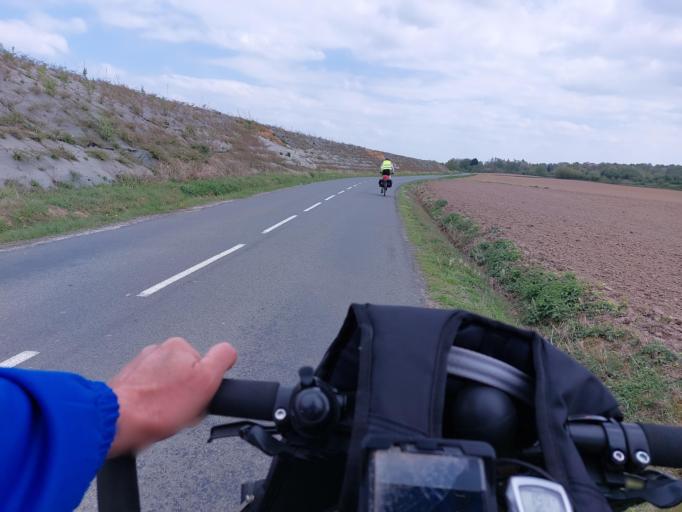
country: FR
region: Nord-Pas-de-Calais
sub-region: Departement du Nord
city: La Longueville
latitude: 50.2806
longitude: 3.8702
